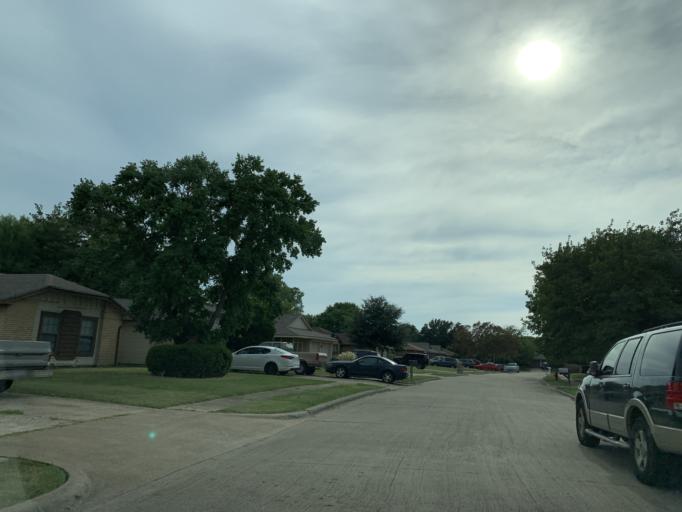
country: US
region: Texas
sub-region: Tarrant County
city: Arlington
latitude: 32.6661
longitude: -97.0461
